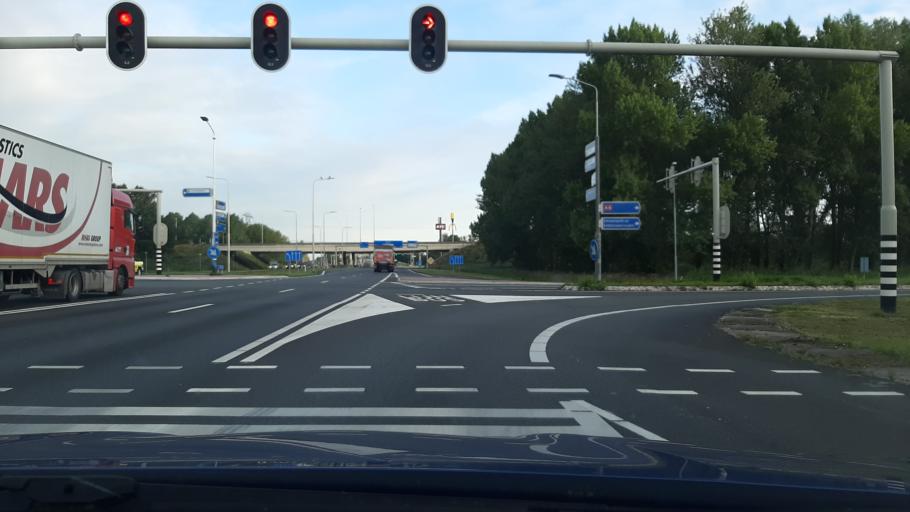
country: NL
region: Flevoland
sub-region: Gemeente Lelystad
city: Lelystad
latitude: 52.4790
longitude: 5.5056
